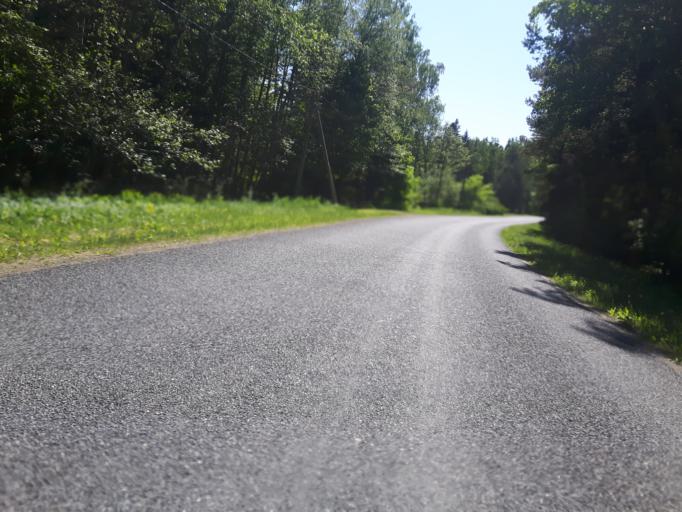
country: EE
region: Laeaene-Virumaa
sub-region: Haljala vald
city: Haljala
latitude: 59.5718
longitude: 26.2657
